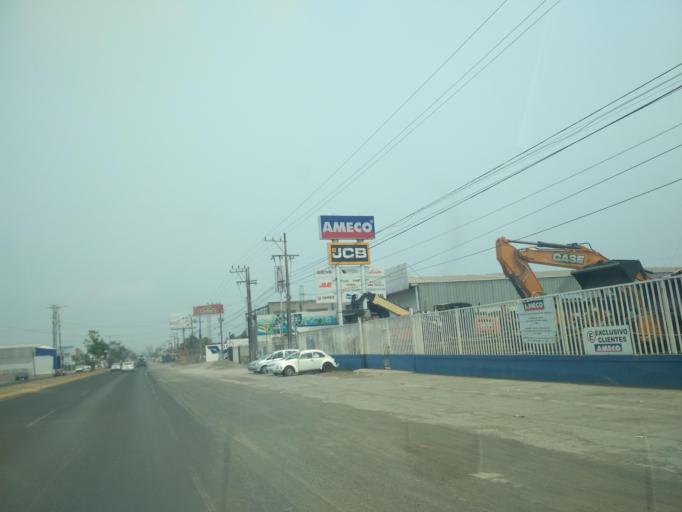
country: MX
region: Veracruz
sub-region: Veracruz
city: Las Amapolas
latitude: 19.1583
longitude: -96.1962
